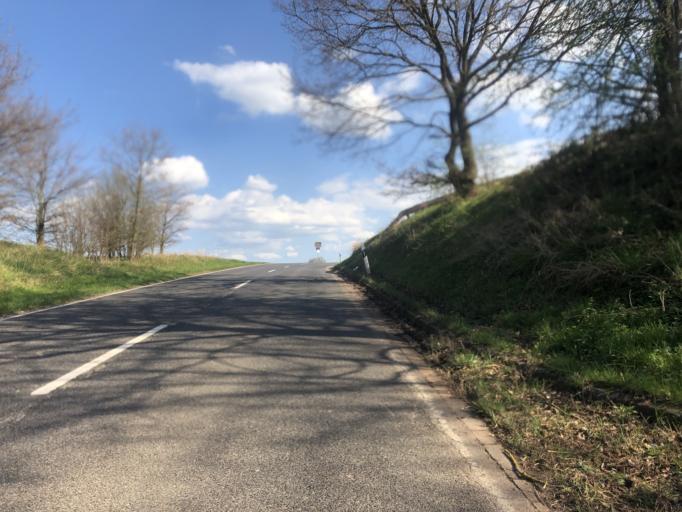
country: DE
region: North Rhine-Westphalia
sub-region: Regierungsbezirk Koln
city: Kall
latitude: 50.5885
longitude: 6.5750
